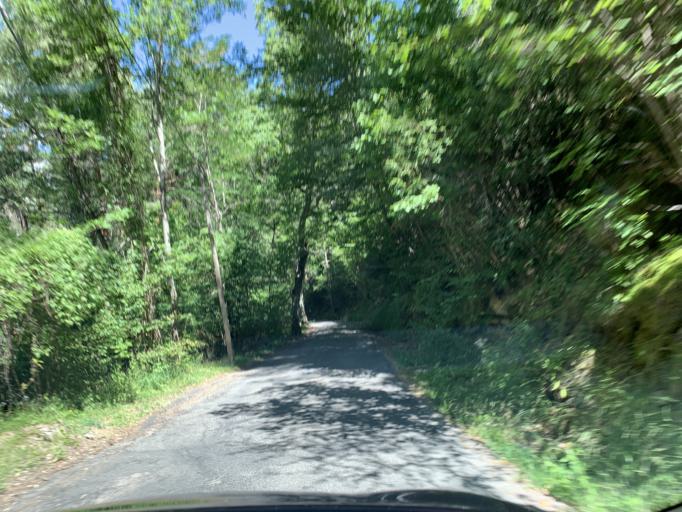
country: ES
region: Aragon
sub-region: Provincia de Huesca
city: Hoz de Jaca
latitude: 42.6970
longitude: -0.3066
